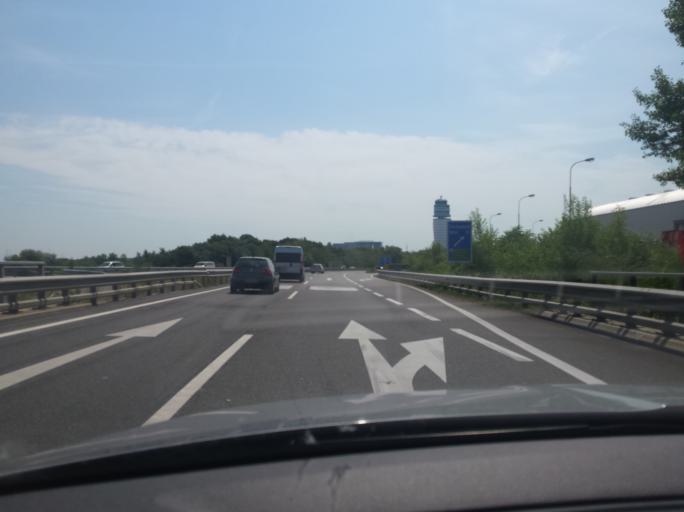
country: AT
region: Lower Austria
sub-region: Politischer Bezirk Wien-Umgebung
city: Rauchenwarth
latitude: 48.1281
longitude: 16.5529
